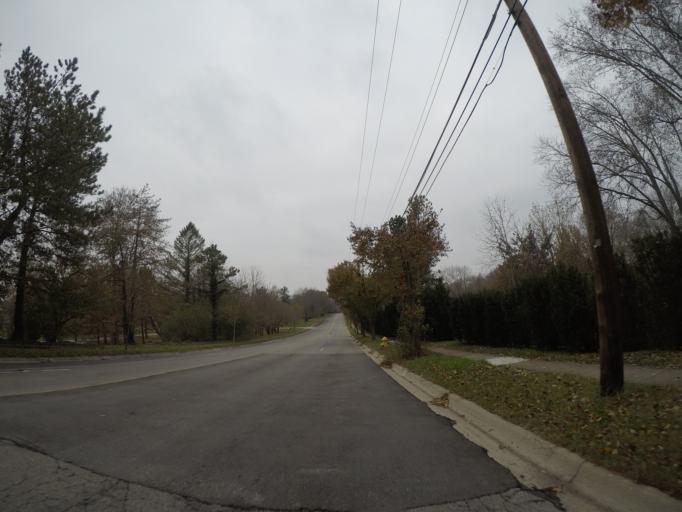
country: US
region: Ohio
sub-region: Franklin County
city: Upper Arlington
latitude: 40.0414
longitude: -83.0893
